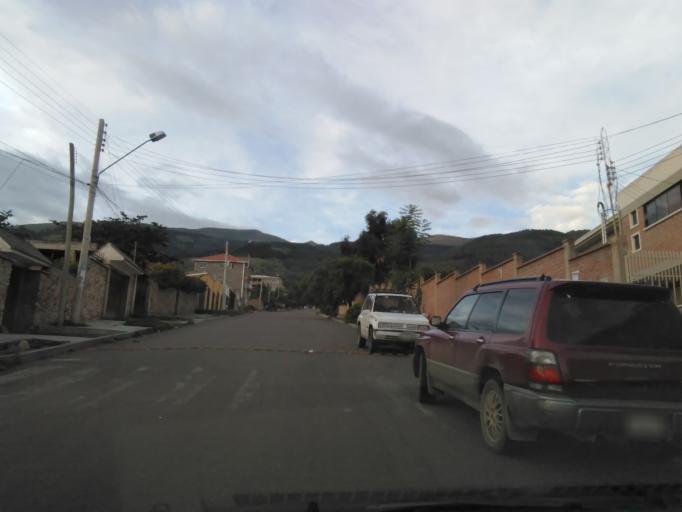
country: BO
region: Cochabamba
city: Cochabamba
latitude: -17.3566
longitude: -66.1554
